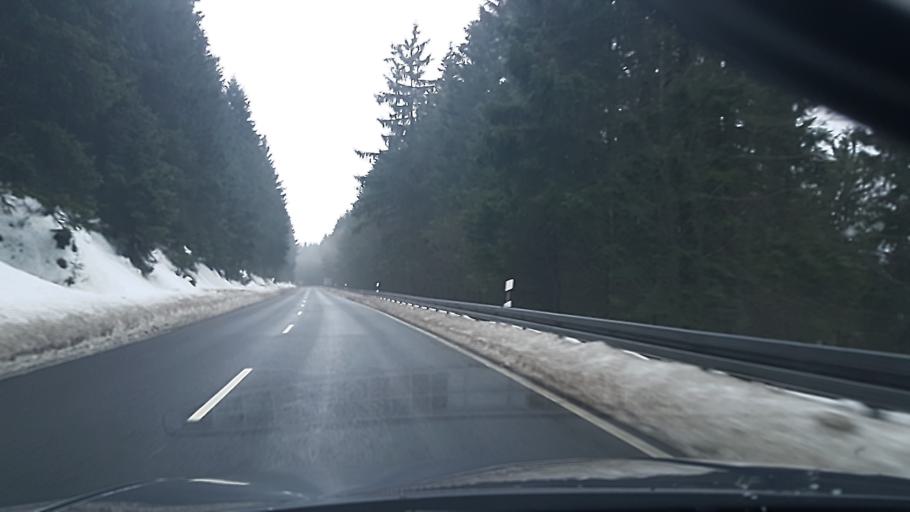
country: DE
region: Lower Saxony
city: Clausthal-Zellerfeld
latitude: 51.8488
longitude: 10.3574
